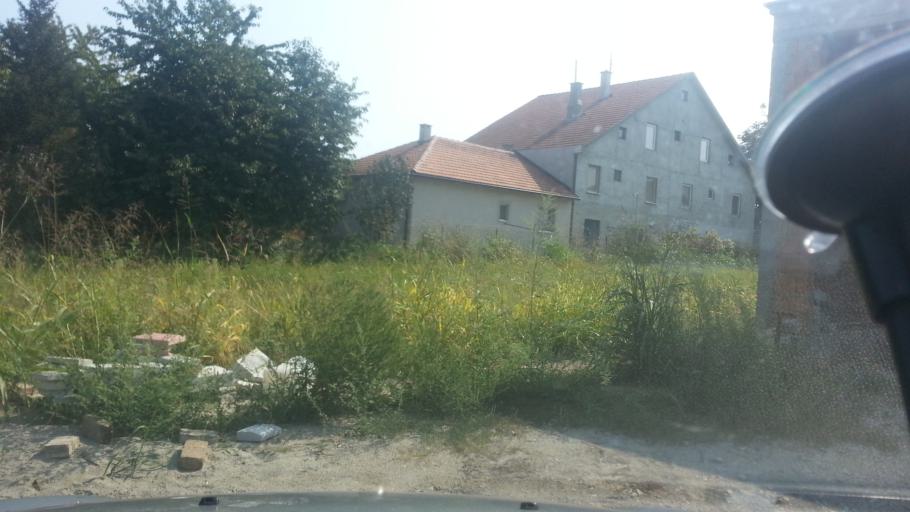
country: RS
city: Novi Banovci
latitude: 44.9444
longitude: 20.2836
